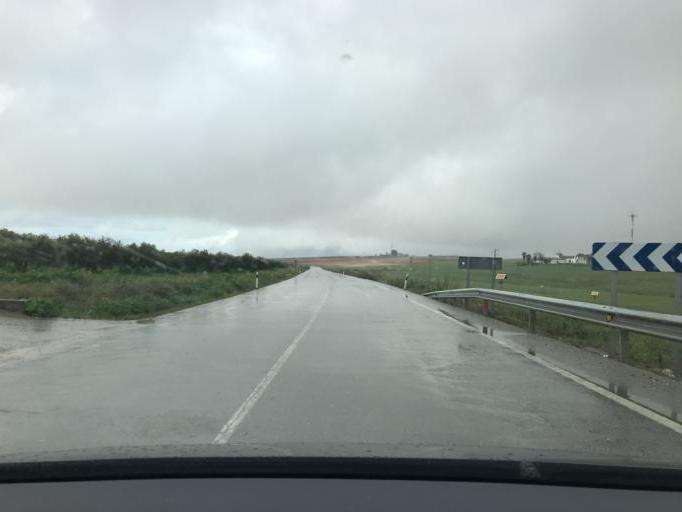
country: ES
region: Andalusia
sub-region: Provincia de Sevilla
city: La Luisiana
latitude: 37.4602
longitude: -5.2148
